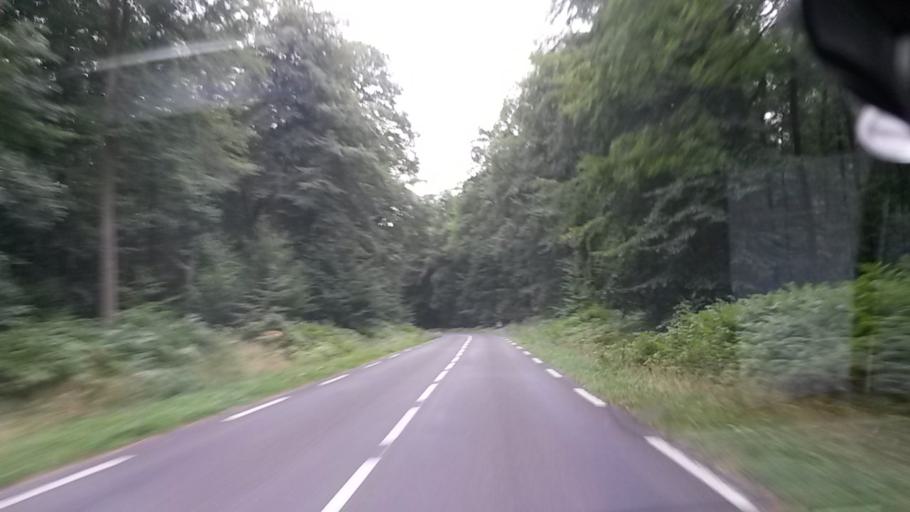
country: FR
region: Haute-Normandie
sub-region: Departement de l'Eure
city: Charleval
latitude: 49.3761
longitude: 1.4646
